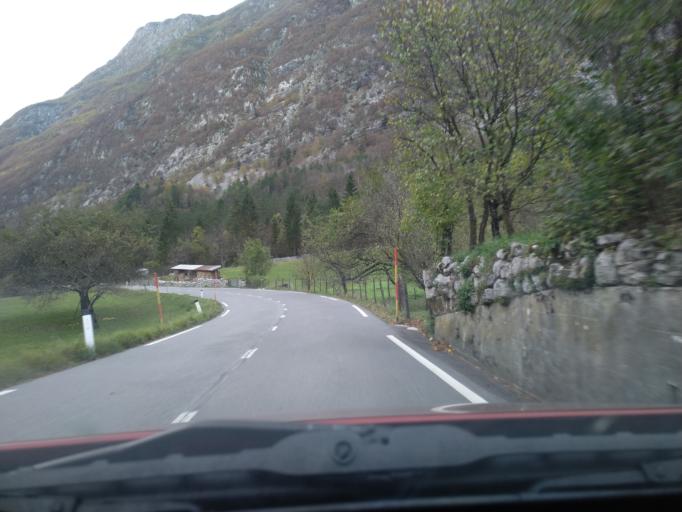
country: SI
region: Bovec
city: Bovec
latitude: 46.3356
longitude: 13.6372
